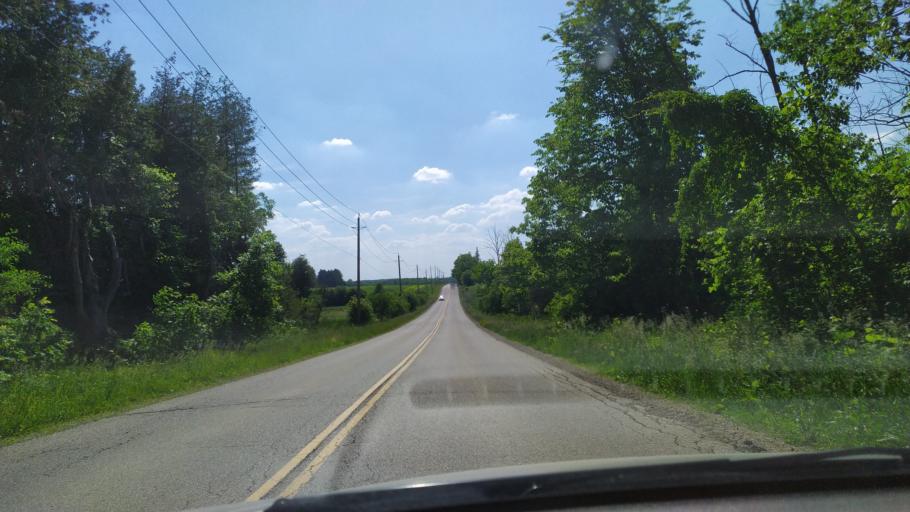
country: CA
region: Ontario
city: Kitchener
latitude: 43.3613
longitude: -80.6235
